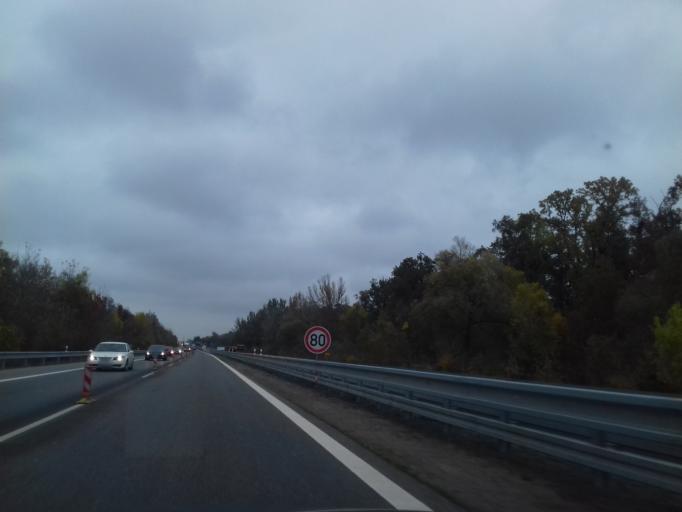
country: CZ
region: South Moravian
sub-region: Okres Breclav
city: Lanzhot
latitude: 48.7120
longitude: 16.9864
